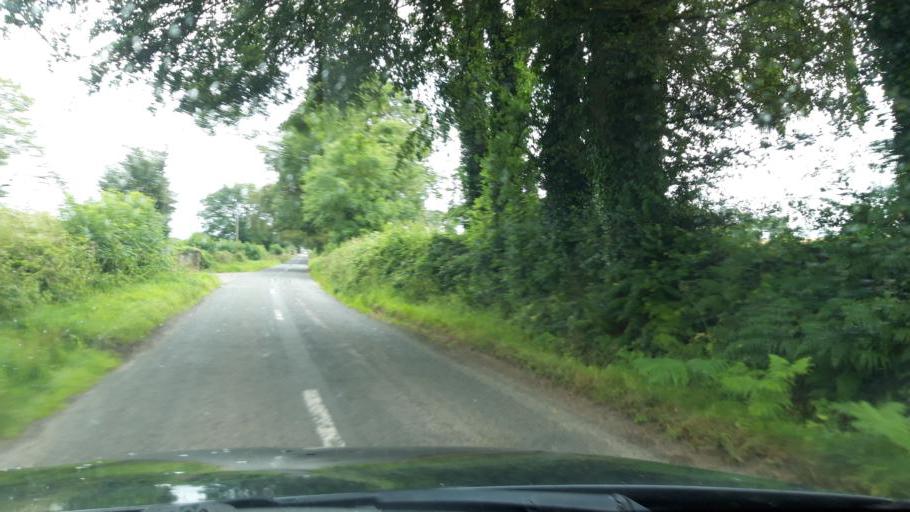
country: IE
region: Munster
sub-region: County Cork
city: Castlemartyr
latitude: 52.1354
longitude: -8.0274
